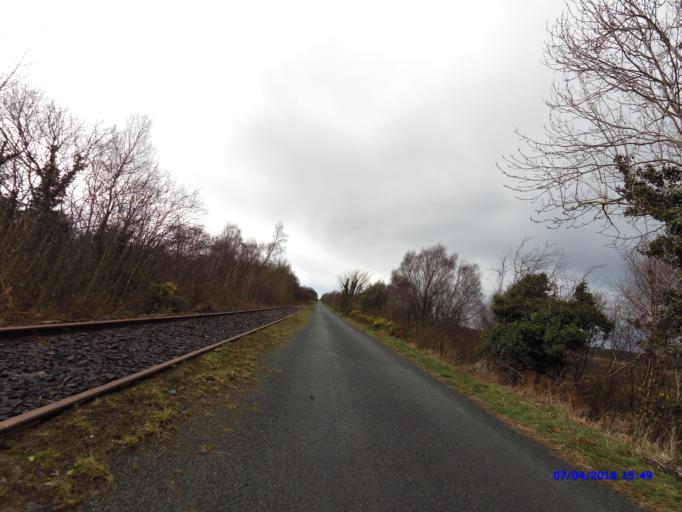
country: IE
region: Leinster
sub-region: An Iarmhi
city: Athlone
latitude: 53.4132
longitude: -7.8481
